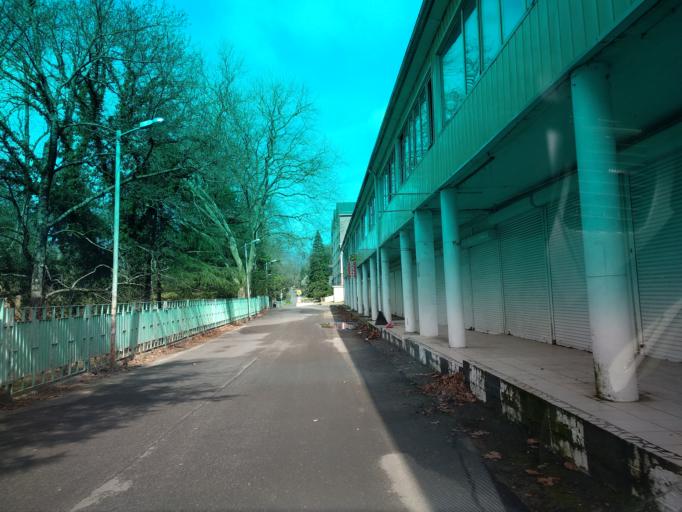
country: RU
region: Krasnodarskiy
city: Shepsi
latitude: 44.0326
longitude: 39.1463
